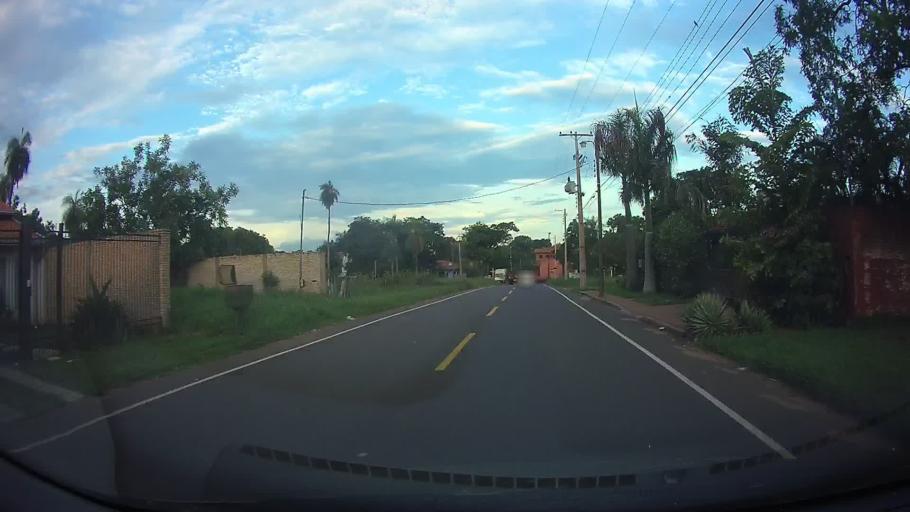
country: PY
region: Central
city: San Lorenzo
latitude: -25.2547
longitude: -57.5015
